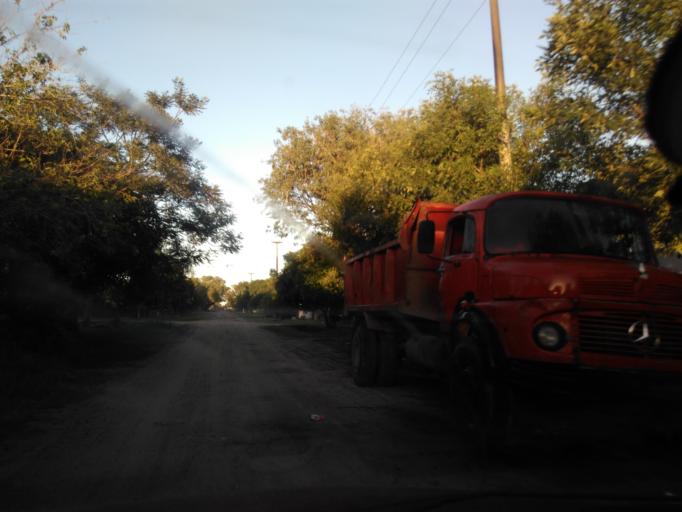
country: AR
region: Chaco
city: Resistencia
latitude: -27.4716
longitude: -59.0024
